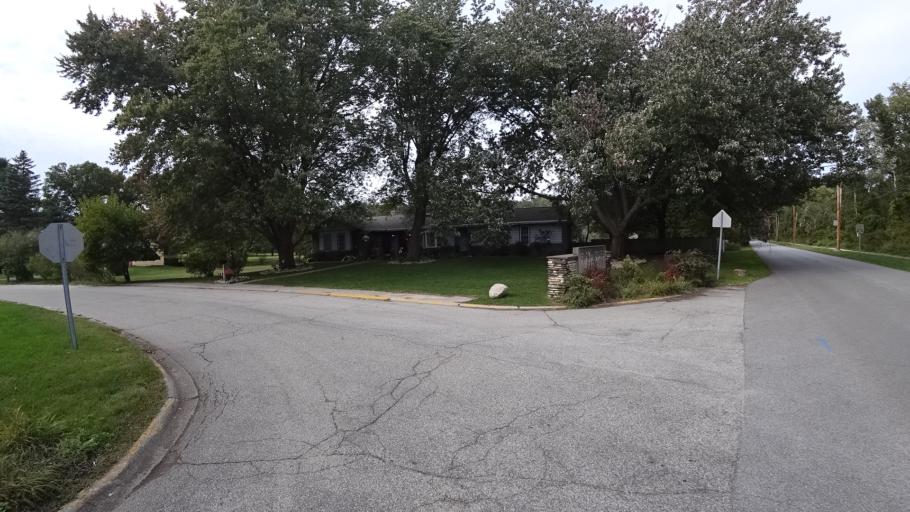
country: US
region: Indiana
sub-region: LaPorte County
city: Long Beach
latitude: 41.7452
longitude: -86.8364
